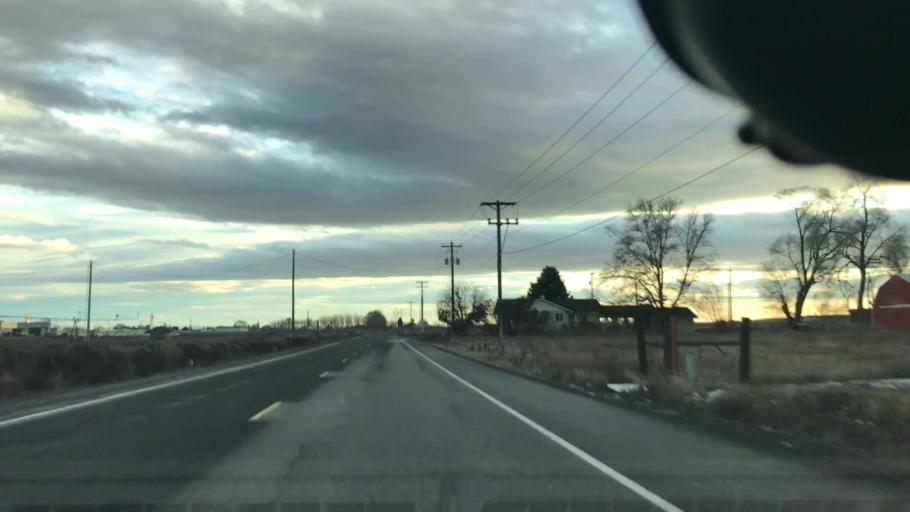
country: US
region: Washington
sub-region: Grant County
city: Moses Lake
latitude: 47.1029
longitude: -119.2362
